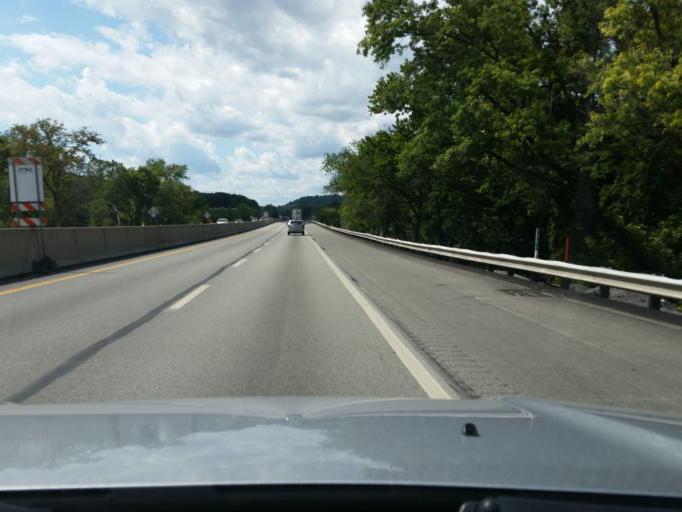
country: US
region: Pennsylvania
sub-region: Bedford County
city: Bedford
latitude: 40.0205
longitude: -78.4768
